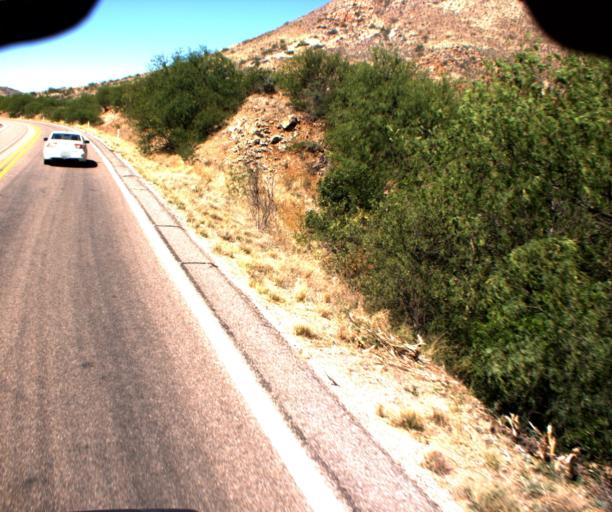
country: US
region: Arizona
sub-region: Santa Cruz County
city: Rio Rico
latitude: 31.5063
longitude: -110.8056
